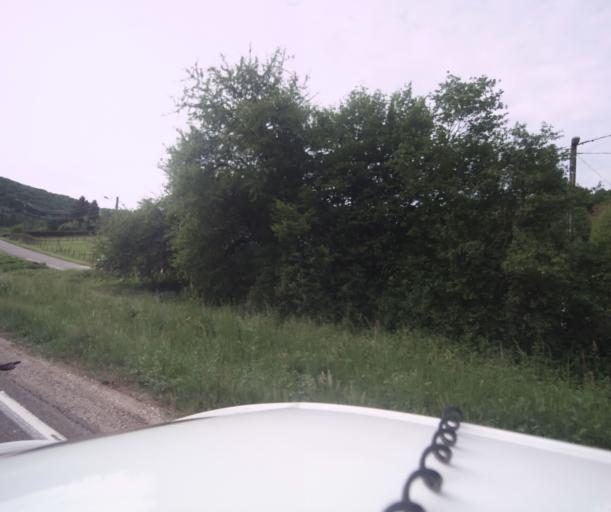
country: FR
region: Franche-Comte
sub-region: Departement du Doubs
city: Beure
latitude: 47.2119
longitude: 5.9934
